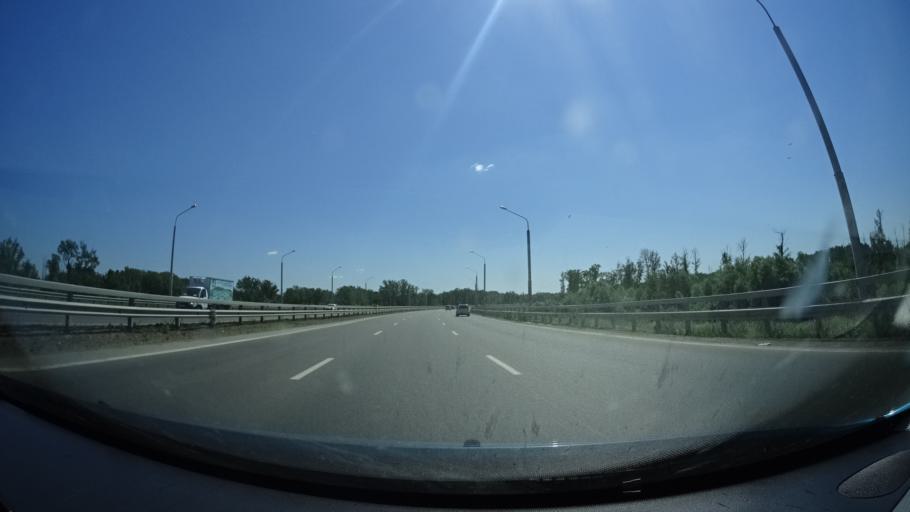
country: RU
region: Bashkortostan
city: Mikhaylovka
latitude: 54.7965
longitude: 55.8992
